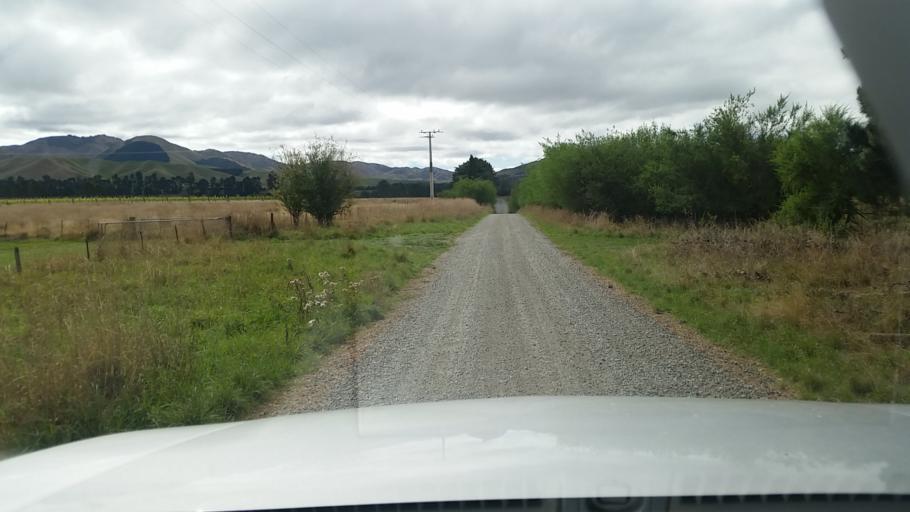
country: NZ
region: Marlborough
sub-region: Marlborough District
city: Blenheim
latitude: -41.6731
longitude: 174.0386
